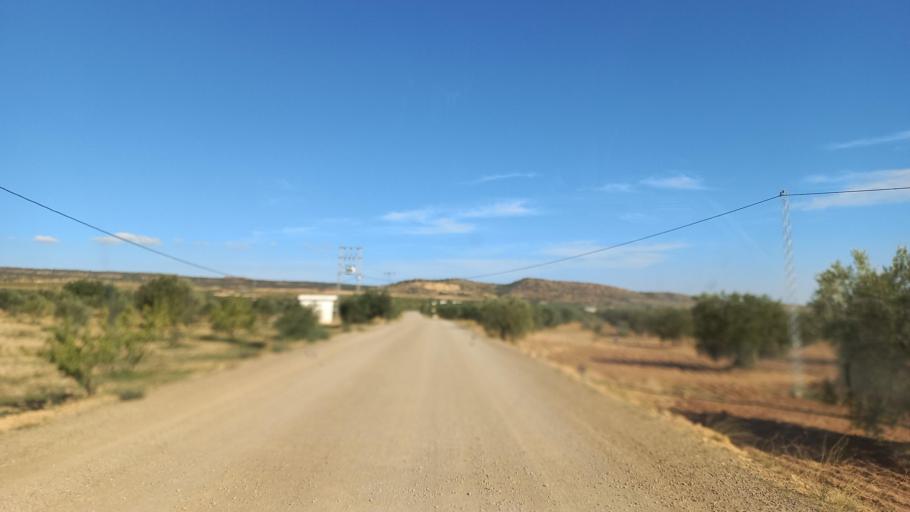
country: TN
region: Al Qasrayn
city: Sbiba
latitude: 35.2961
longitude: 9.1020
